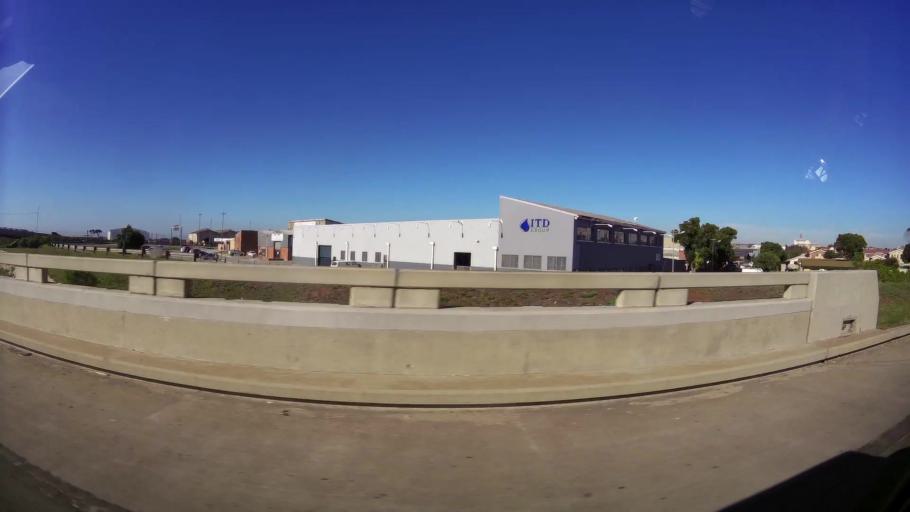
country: ZA
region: Eastern Cape
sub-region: Nelson Mandela Bay Metropolitan Municipality
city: Port Elizabeth
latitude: -33.9140
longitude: 25.6009
